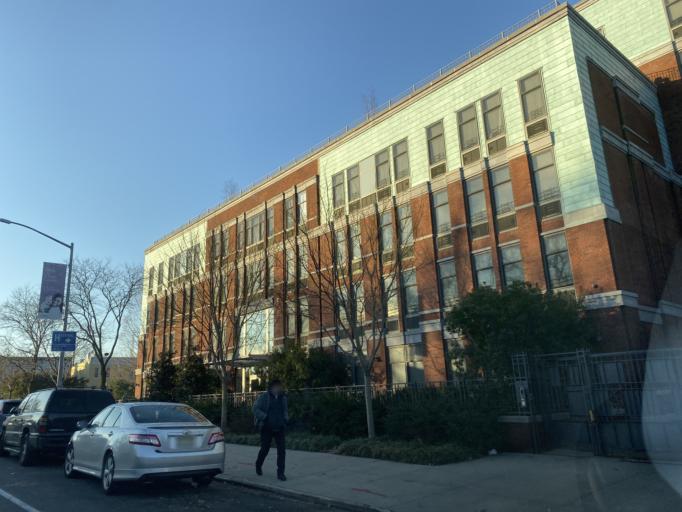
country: US
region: New York
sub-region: Kings County
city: Brooklyn
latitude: 40.6567
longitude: -73.9397
